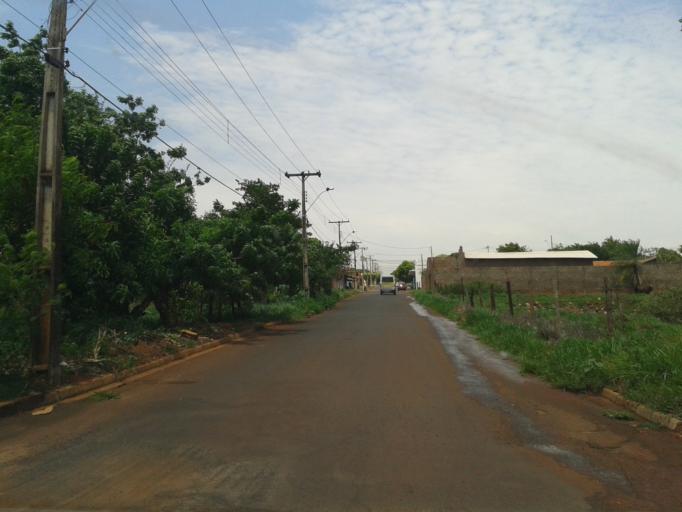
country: BR
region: Minas Gerais
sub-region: Ituiutaba
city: Ituiutaba
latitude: -18.9915
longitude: -49.4412
